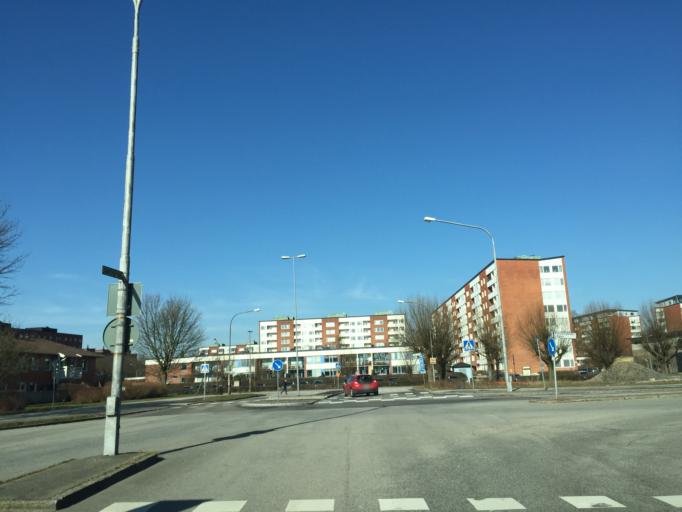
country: SE
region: Skane
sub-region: Lunds Kommun
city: Lund
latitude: 55.6893
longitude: 13.1821
